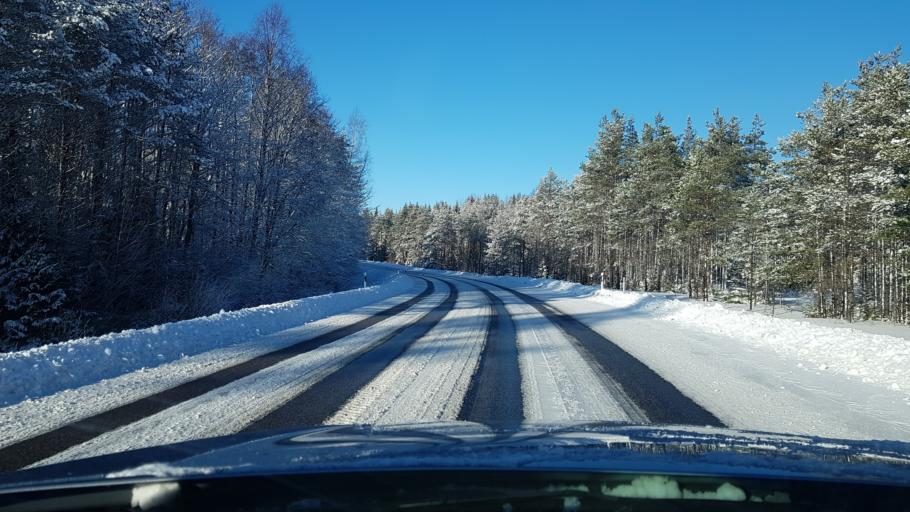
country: EE
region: Hiiumaa
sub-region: Kaerdla linn
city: Kardla
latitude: 58.9716
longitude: 22.7681
